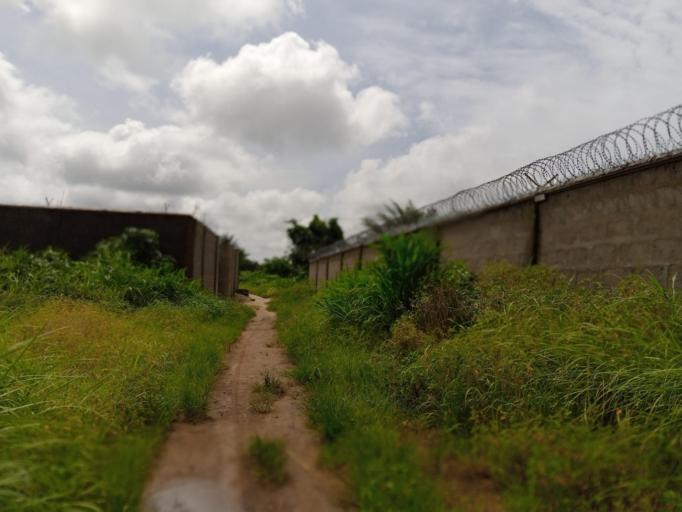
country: SL
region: Northern Province
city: Masoyila
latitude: 8.5920
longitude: -13.1944
